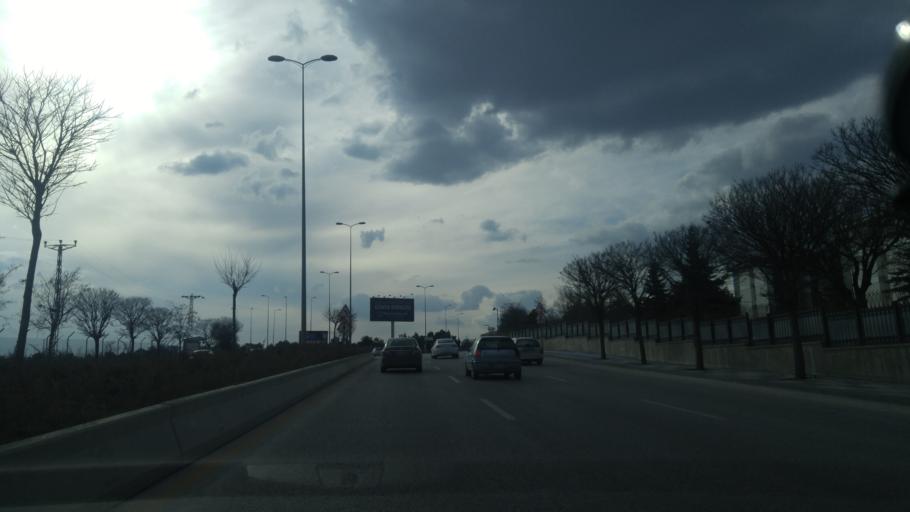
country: TR
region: Ankara
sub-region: Goelbasi
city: Golbasi
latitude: 39.8442
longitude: 32.7844
